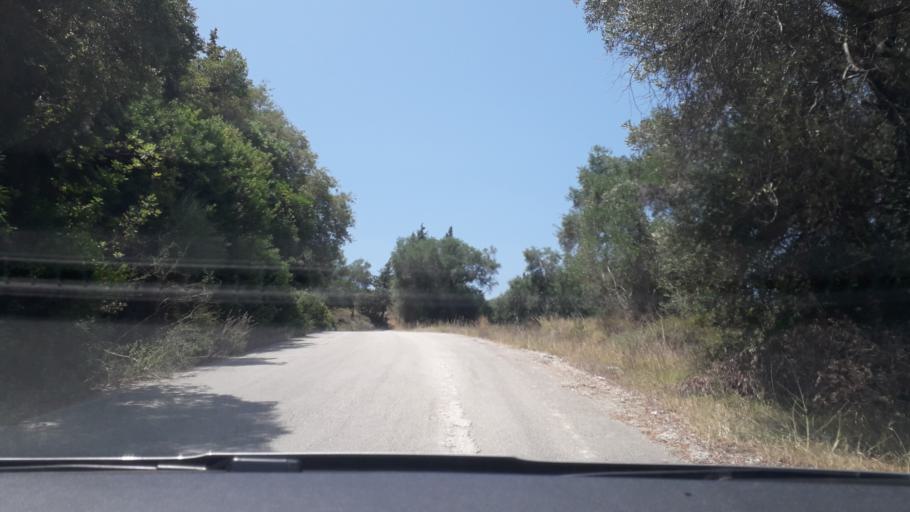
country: GR
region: Ionian Islands
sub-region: Nomos Kerkyras
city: Lefkimmi
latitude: 39.3797
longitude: 20.1071
